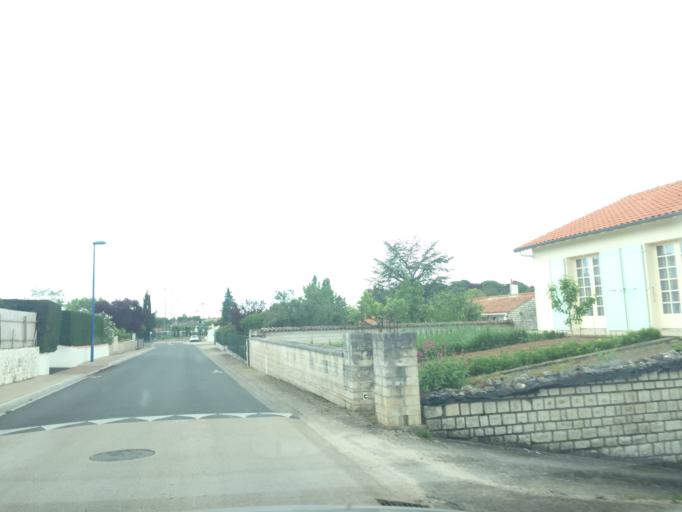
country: FR
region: Pays de la Loire
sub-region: Departement de la Vendee
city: Benet
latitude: 46.3727
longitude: -0.5852
